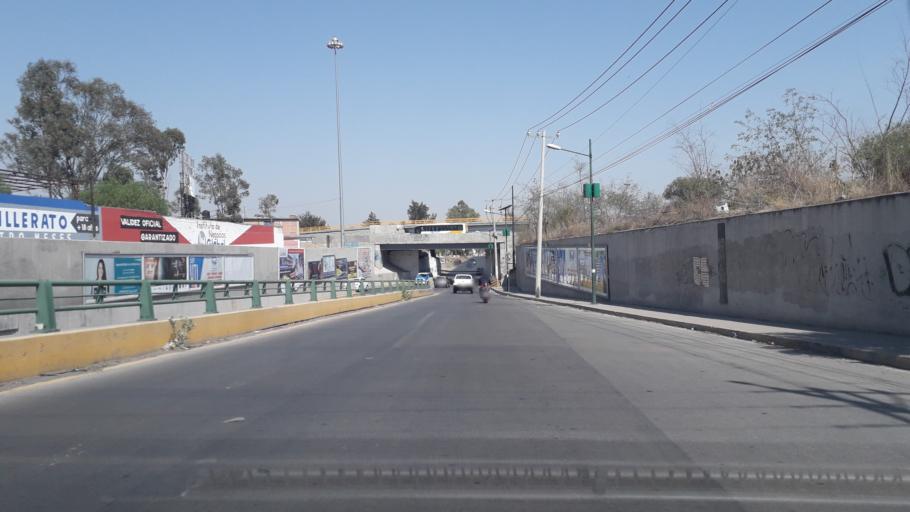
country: MX
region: Mexico
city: Santo Tomas Chiconautla
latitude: 19.6603
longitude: -99.0055
